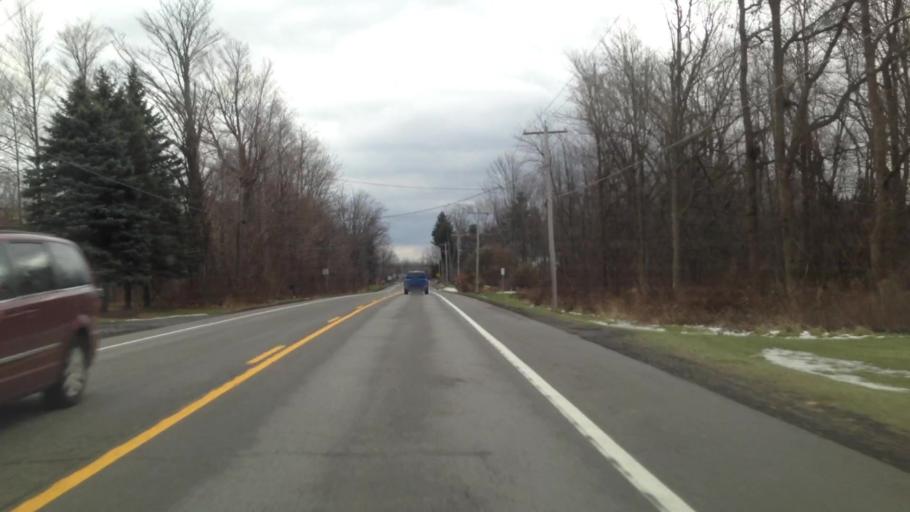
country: US
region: New York
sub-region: Erie County
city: Akron
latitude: 42.9981
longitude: -78.4684
